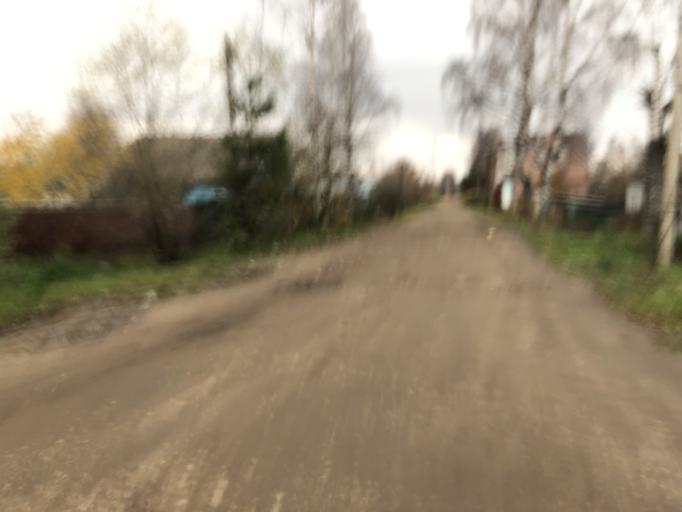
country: RU
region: Tverskaya
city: Rzhev
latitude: 56.2527
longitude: 34.3242
